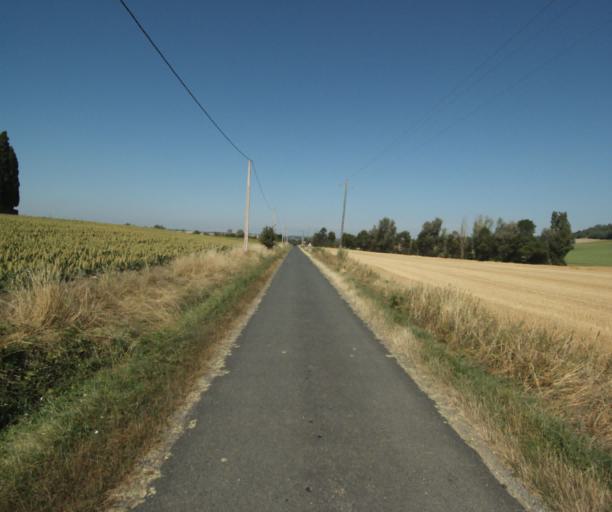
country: FR
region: Midi-Pyrenees
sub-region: Departement de la Haute-Garonne
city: Saint-Felix-Lauragais
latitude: 43.5089
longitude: 1.9275
